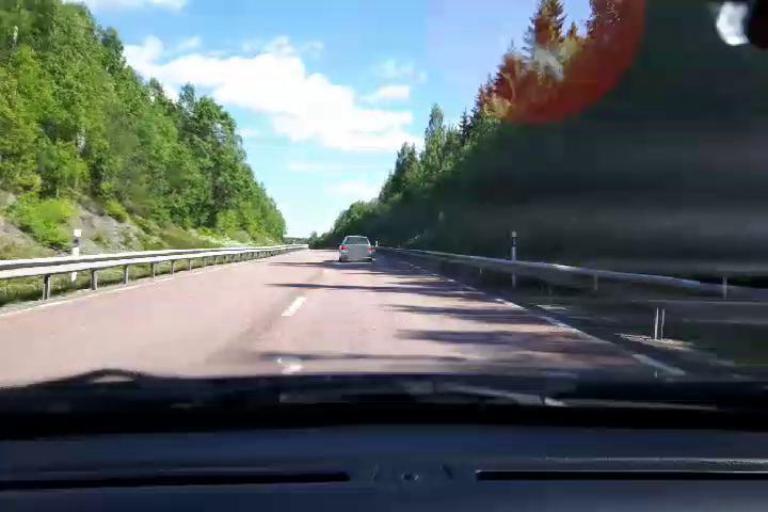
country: SE
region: Gaevleborg
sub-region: Hudiksvalls Kommun
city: Sorforsa
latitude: 61.7407
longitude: 16.8655
